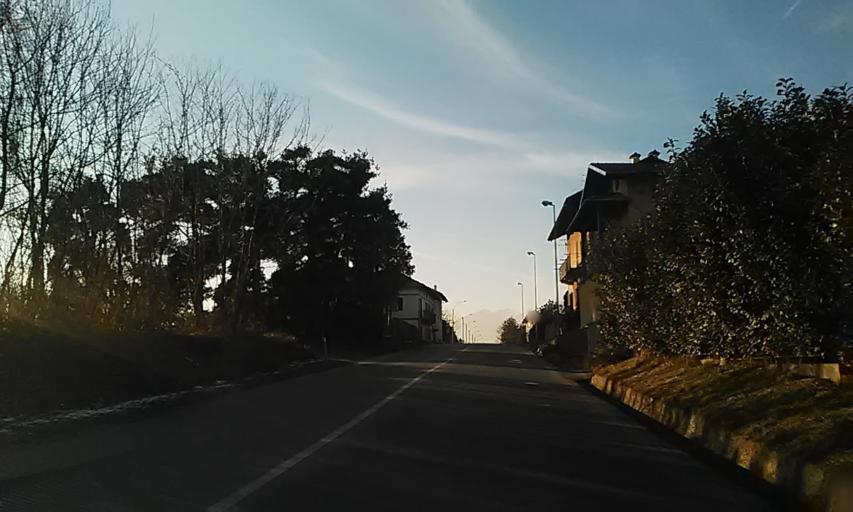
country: IT
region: Piedmont
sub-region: Provincia di Biella
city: Masserano
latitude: 45.5675
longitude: 8.2175
